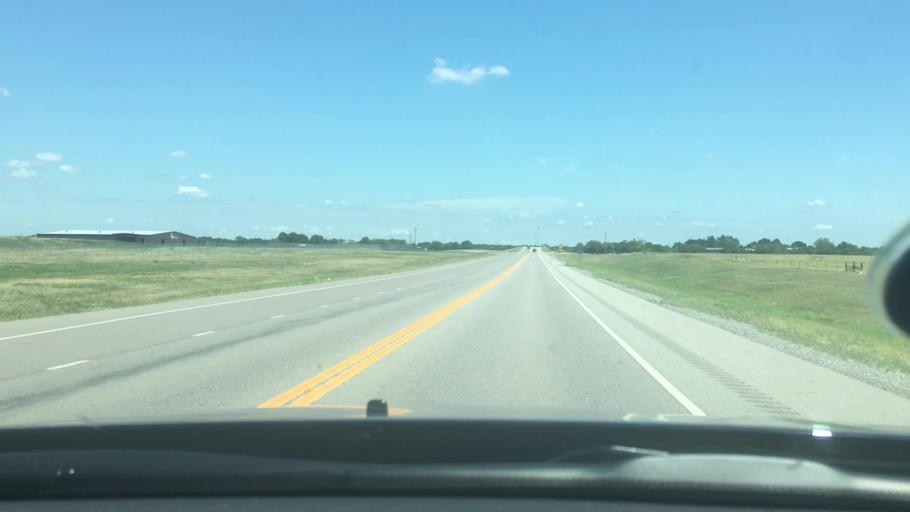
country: US
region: Oklahoma
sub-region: Bryan County
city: Durant
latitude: 33.9789
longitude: -96.3396
